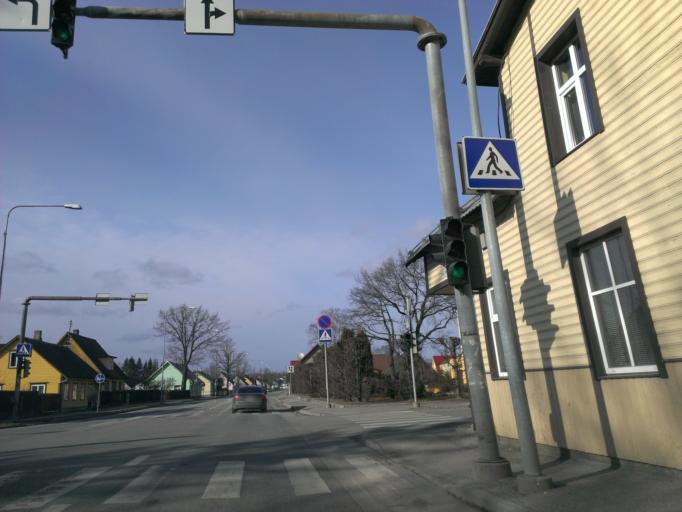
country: EE
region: Paernumaa
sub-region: Paernu linn
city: Parnu
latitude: 58.3990
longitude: 24.4934
